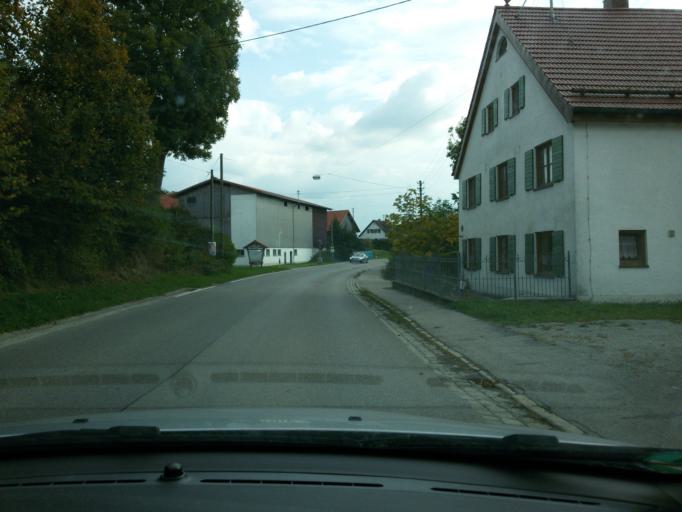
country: DE
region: Bavaria
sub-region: Swabia
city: Buchloe
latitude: 48.0585
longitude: 10.7316
